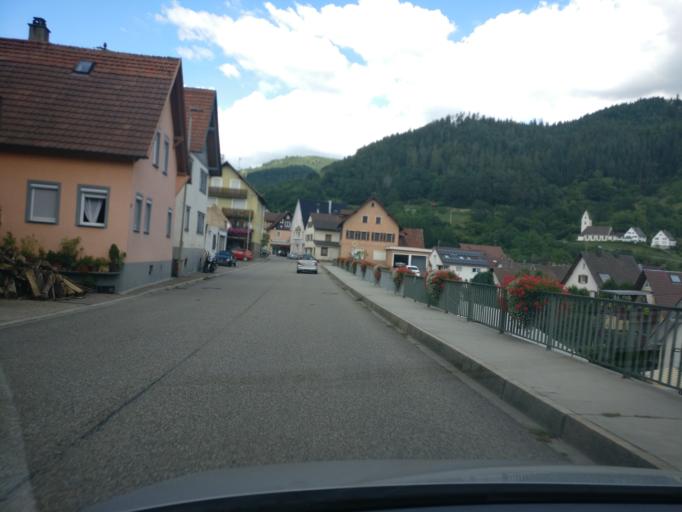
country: DE
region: Baden-Wuerttemberg
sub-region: Karlsruhe Region
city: Forbach
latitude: 48.6765
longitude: 8.3572
